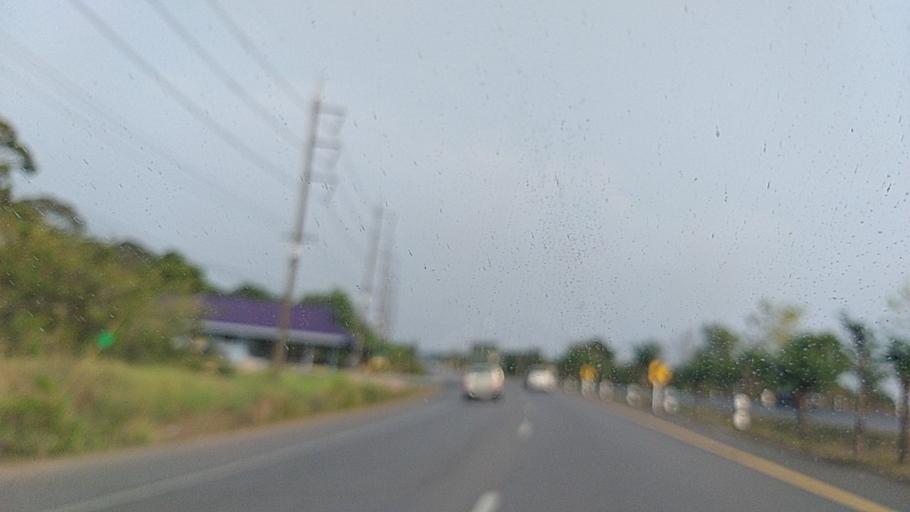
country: TH
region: Chanthaburi
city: Khlung
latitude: 12.4482
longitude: 102.2880
